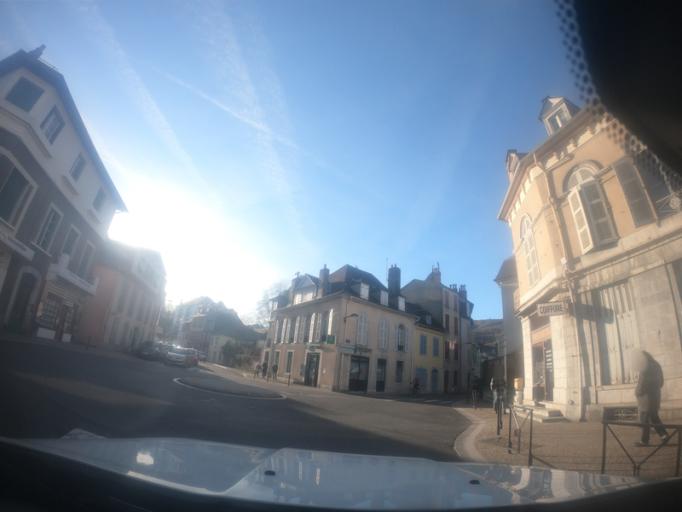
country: FR
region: Midi-Pyrenees
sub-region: Departement des Hautes-Pyrenees
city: Bagneres-de-Bigorre
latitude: 43.0626
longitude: 0.1500
